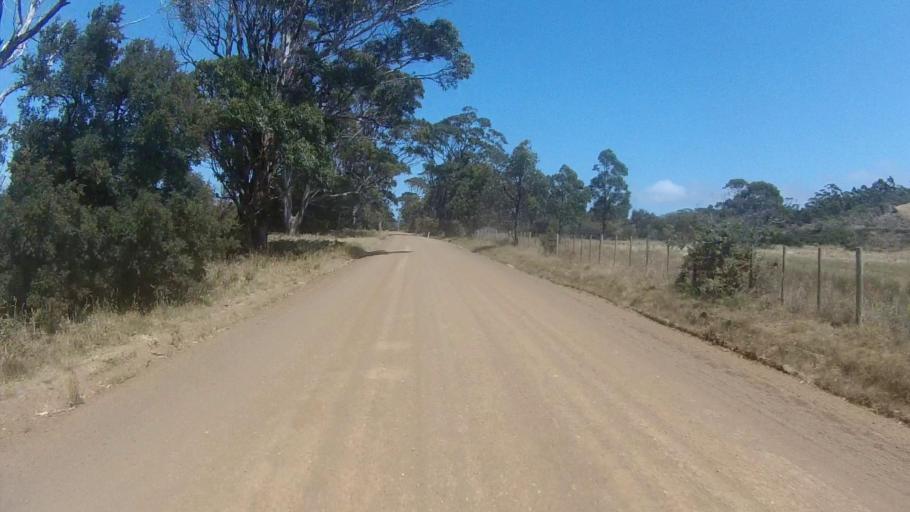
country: AU
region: Tasmania
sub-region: Sorell
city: Sorell
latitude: -42.8322
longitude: 147.8559
